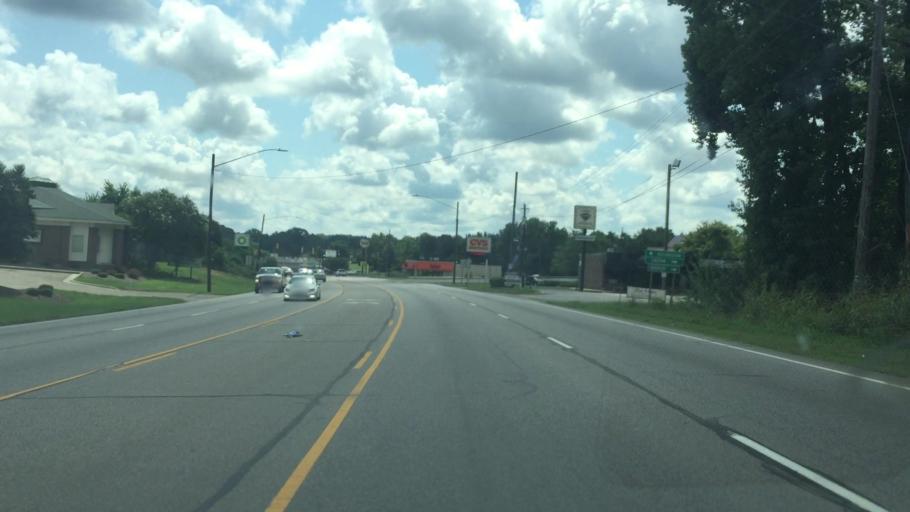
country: US
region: North Carolina
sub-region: Anson County
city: Wadesboro
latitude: 34.9644
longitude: -80.0589
